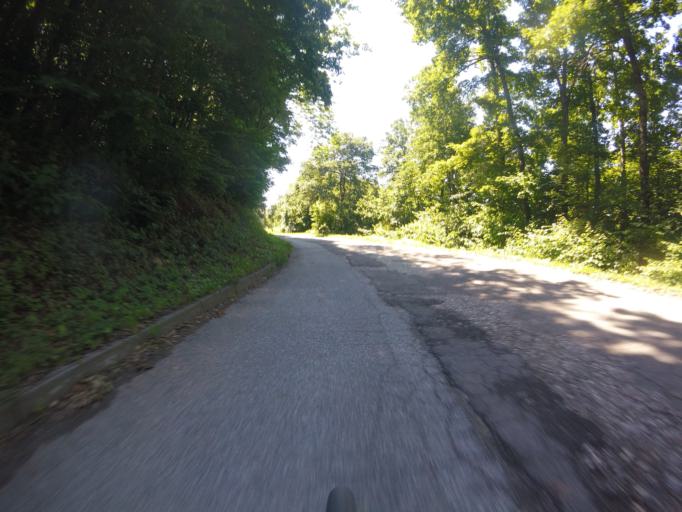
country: SI
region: Kostanjevica na Krki
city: Kostanjevica na Krki
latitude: 45.7998
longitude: 15.4941
